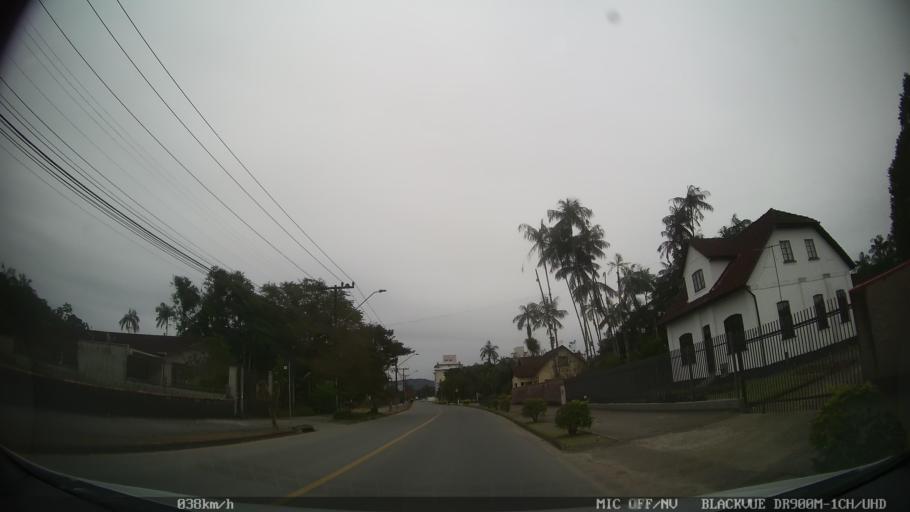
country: BR
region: Santa Catarina
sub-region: Joinville
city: Joinville
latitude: -26.2017
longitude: -48.9076
